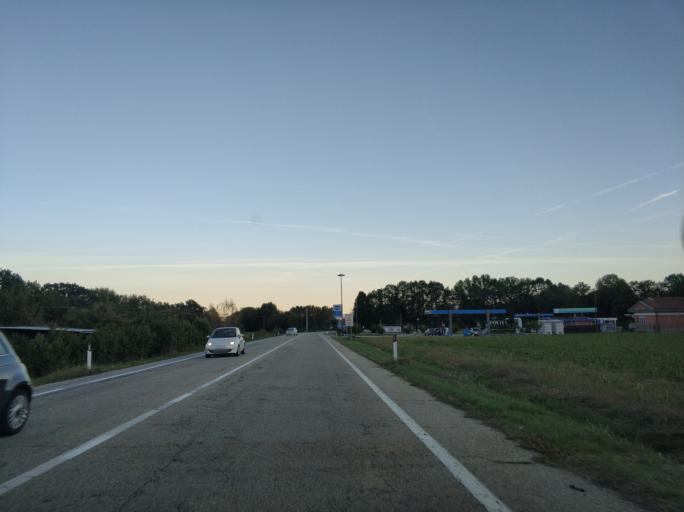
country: IT
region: Piedmont
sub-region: Provincia di Torino
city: Fiano
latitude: 45.2149
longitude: 7.5427
